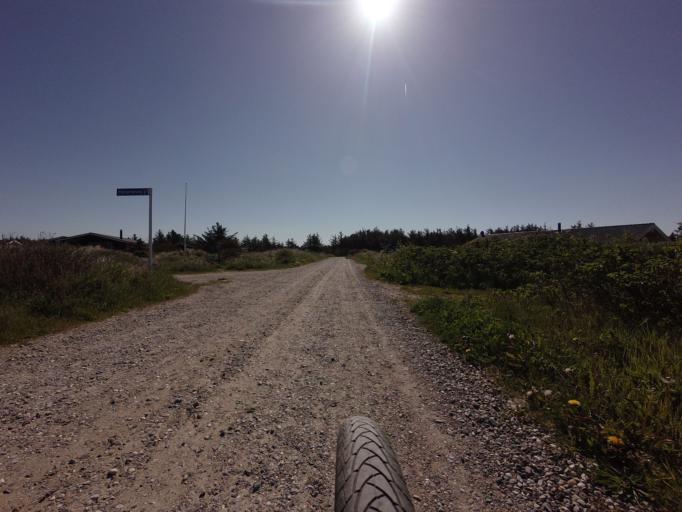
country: DK
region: North Denmark
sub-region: Jammerbugt Kommune
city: Pandrup
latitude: 57.3351
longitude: 9.6781
